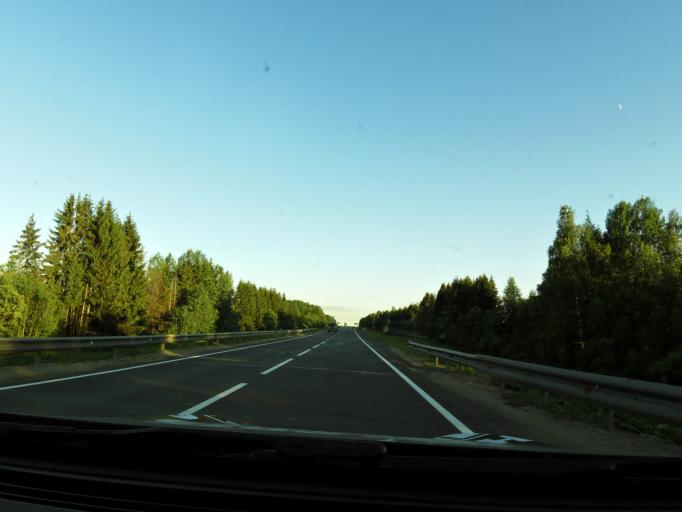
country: RU
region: Vologda
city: Gryazovets
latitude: 58.7219
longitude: 40.2961
